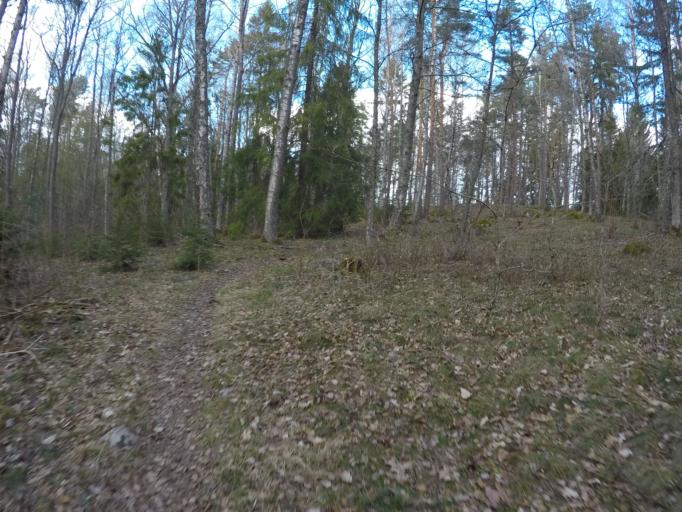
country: SE
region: Soedermanland
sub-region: Eskilstuna Kommun
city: Kvicksund
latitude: 59.4944
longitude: 16.2800
